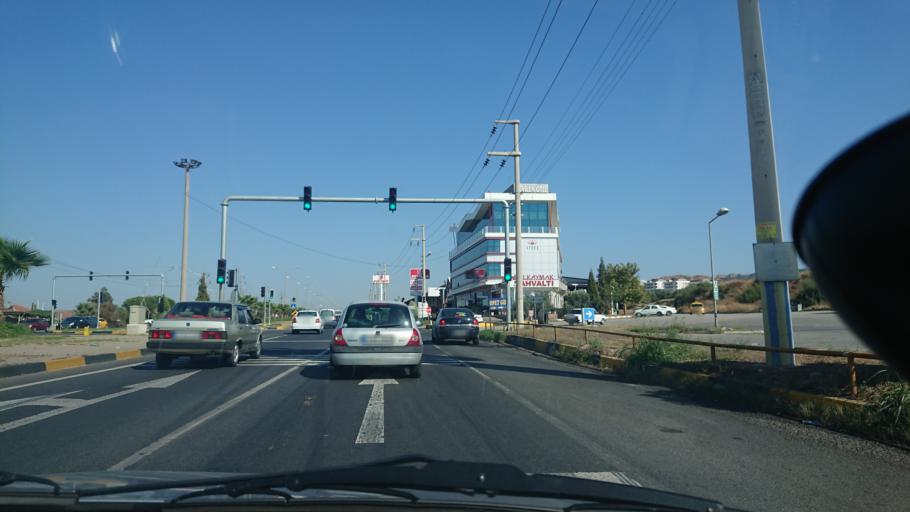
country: TR
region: Manisa
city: Turgutlu
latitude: 38.4957
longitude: 27.7345
